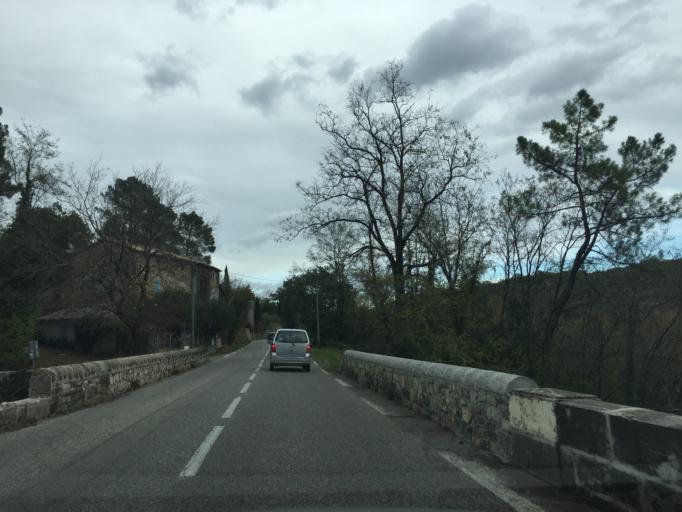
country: FR
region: Rhone-Alpes
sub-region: Departement de l'Ardeche
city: Les Vans
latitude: 44.4241
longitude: 4.1779
